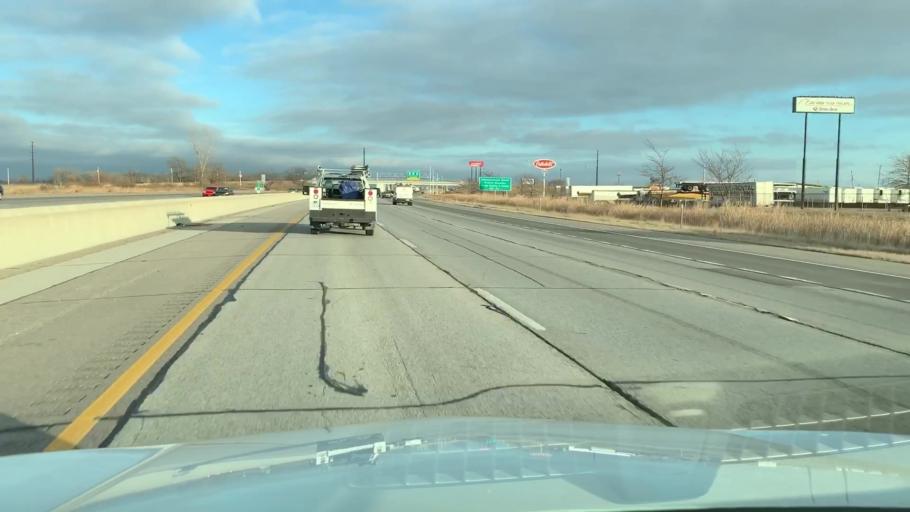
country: US
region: Iowa
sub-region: Polk County
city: Altoona
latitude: 41.6618
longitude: -93.5088
